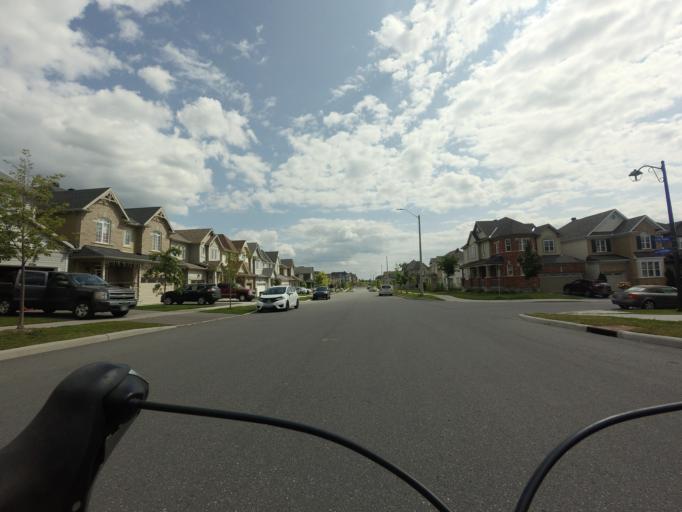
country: CA
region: Ontario
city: Bells Corners
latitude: 45.2766
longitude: -75.8476
